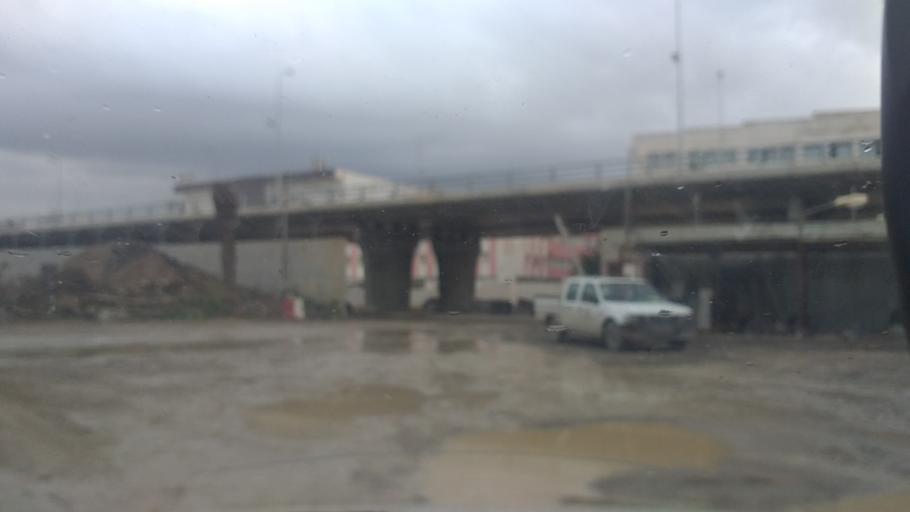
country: TN
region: Ariana
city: Ariana
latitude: 36.8511
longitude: 10.2123
